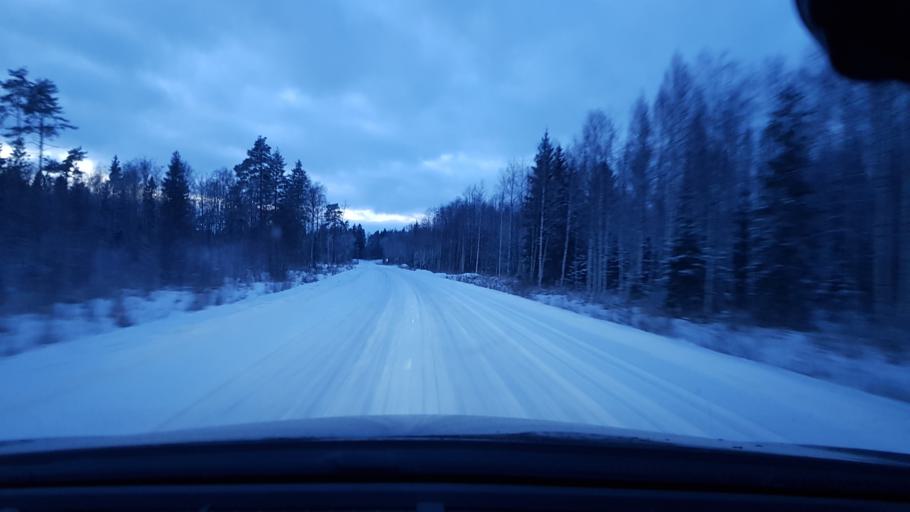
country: EE
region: Harju
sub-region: Nissi vald
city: Turba
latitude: 59.1280
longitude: 24.0796
